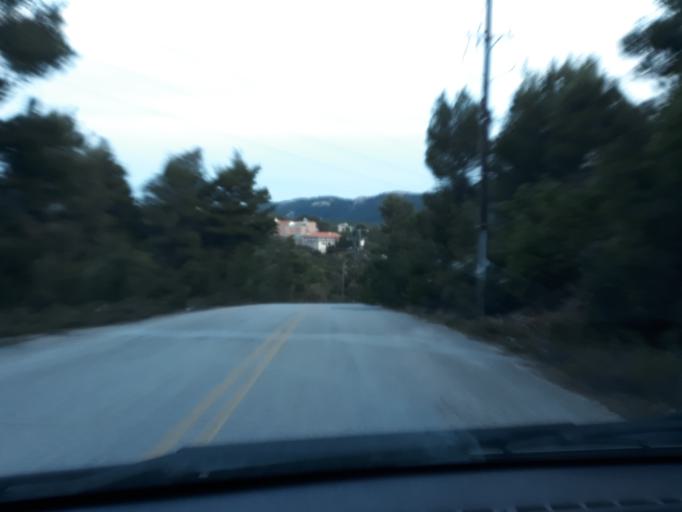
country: GR
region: Attica
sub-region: Nomarchia Anatolikis Attikis
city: Afidnes
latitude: 38.1974
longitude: 23.7923
